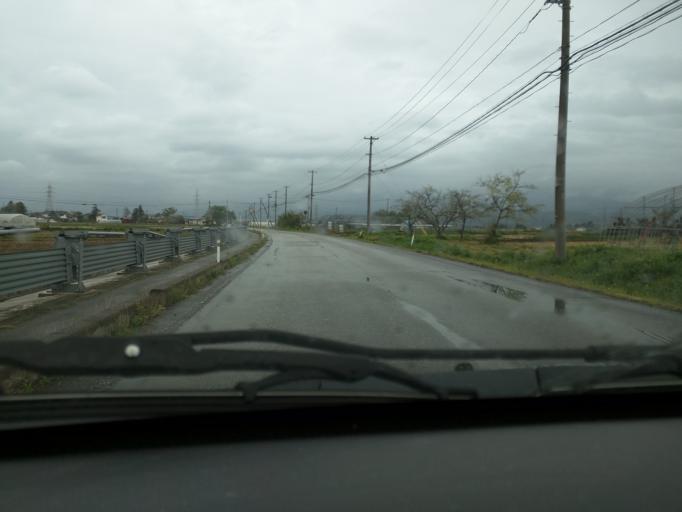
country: JP
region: Fukushima
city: Kitakata
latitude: 37.5708
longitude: 139.8748
